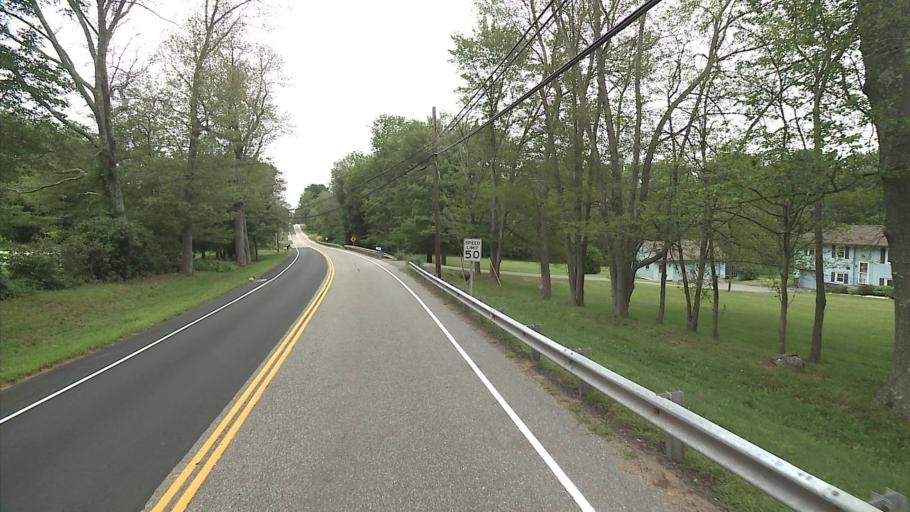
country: US
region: Connecticut
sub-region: Hartford County
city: Manchester
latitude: 41.7321
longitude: -72.4350
